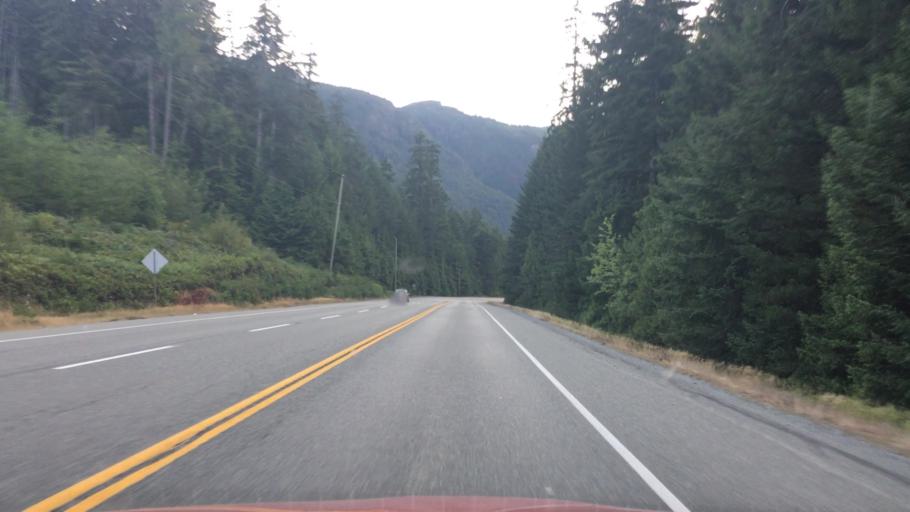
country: CA
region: British Columbia
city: Port Alberni
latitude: 49.2950
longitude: -124.5635
